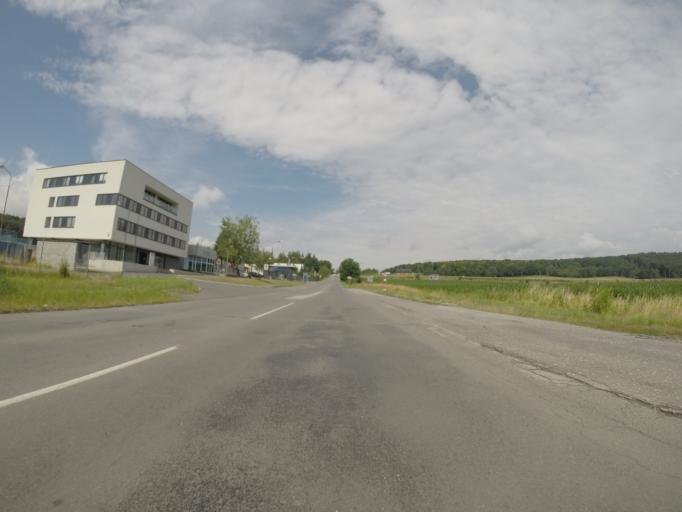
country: SK
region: Banskobystricky
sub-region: Okres Banska Bystrica
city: Zvolen
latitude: 48.5845
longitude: 19.0975
